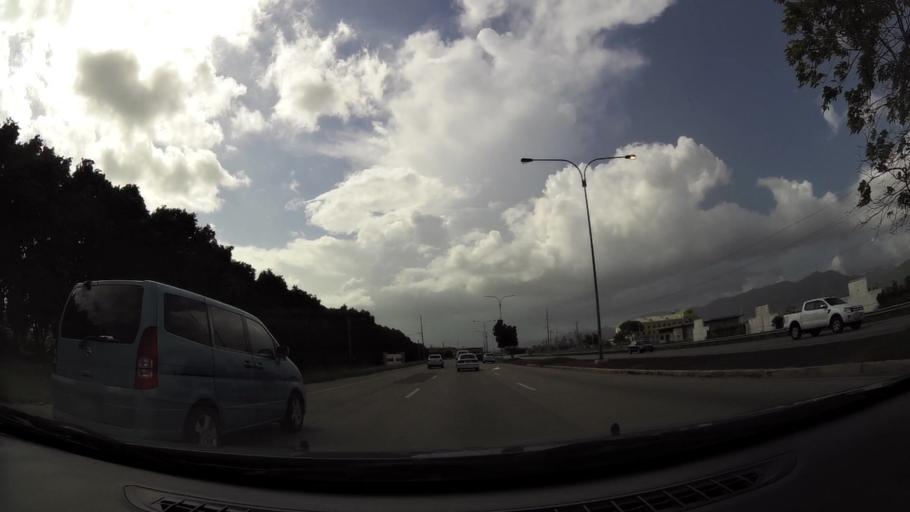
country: TT
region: Tunapuna/Piarco
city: Arouca
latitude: 10.6169
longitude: -61.3480
